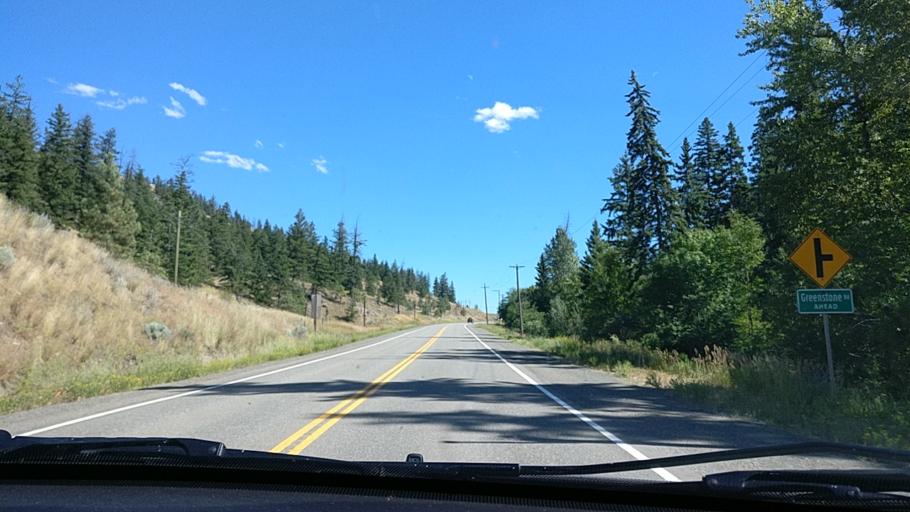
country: CA
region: British Columbia
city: Kamloops
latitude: 50.6693
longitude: -120.5661
